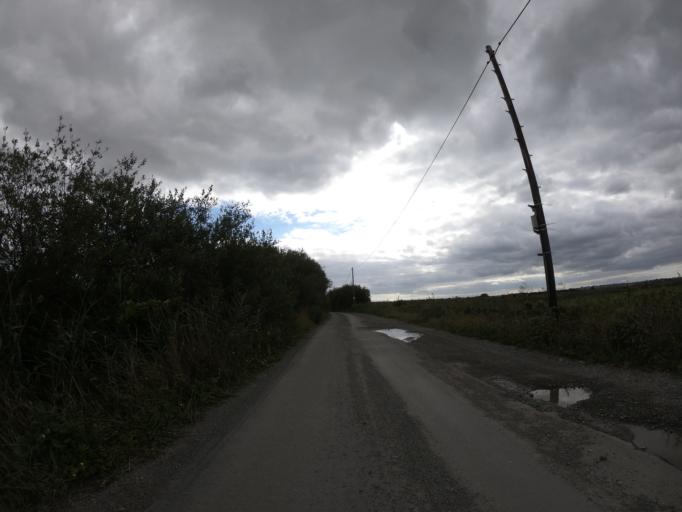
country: GB
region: England
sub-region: Kent
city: Dartford
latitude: 51.4701
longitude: 0.2170
